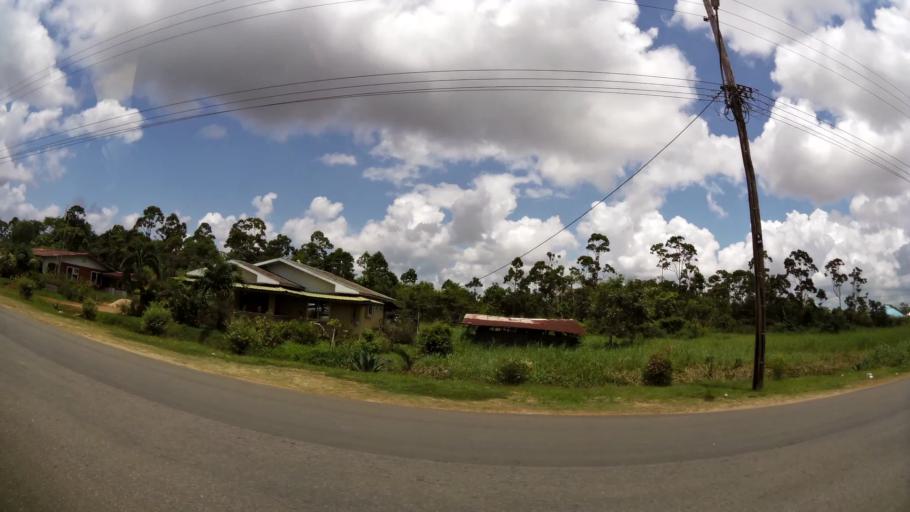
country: SR
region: Paramaribo
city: Paramaribo
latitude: 5.8035
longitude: -55.1246
